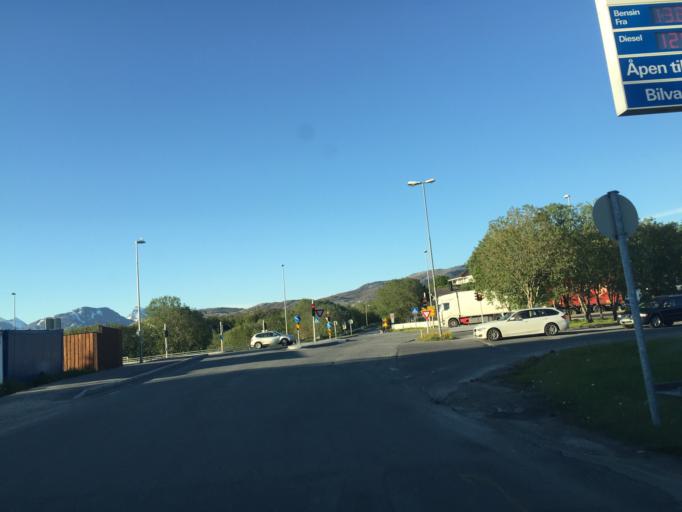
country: NO
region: Nordland
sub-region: Bodo
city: Loding
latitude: 67.3002
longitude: 14.7373
